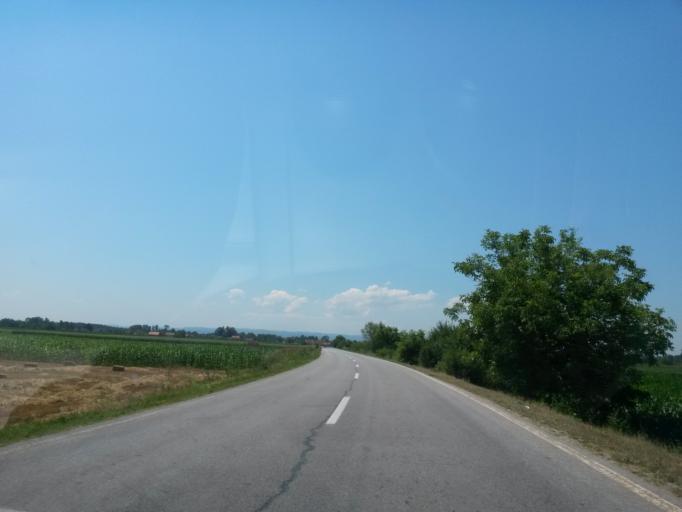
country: BA
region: Federation of Bosnia and Herzegovina
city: Odzak
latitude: 45.0002
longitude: 18.3869
